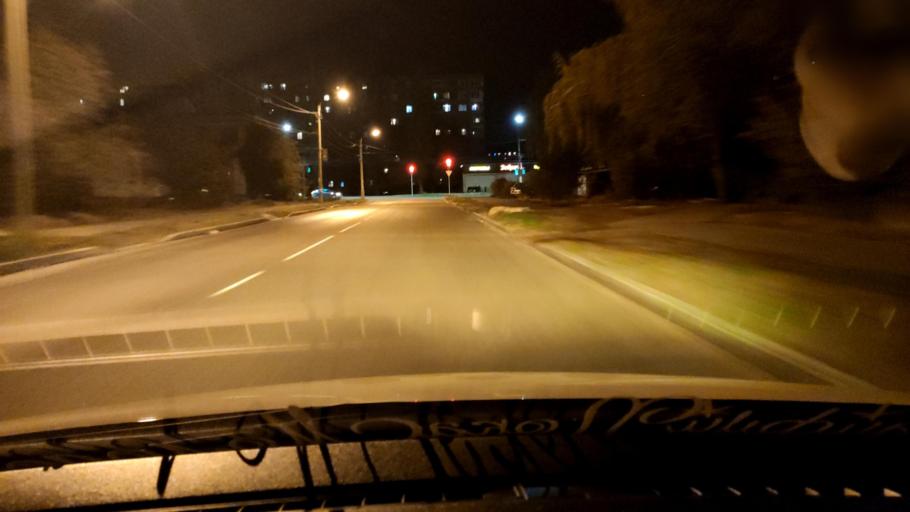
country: RU
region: Voronezj
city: Podgornoye
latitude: 51.7005
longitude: 39.1565
